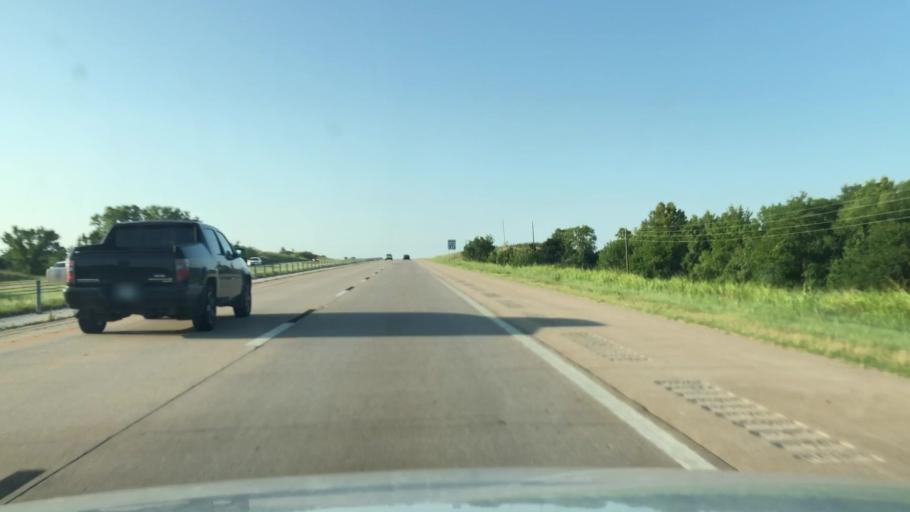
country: US
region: Oklahoma
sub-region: Osage County
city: Skiatook
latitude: 36.5248
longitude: -95.9266
